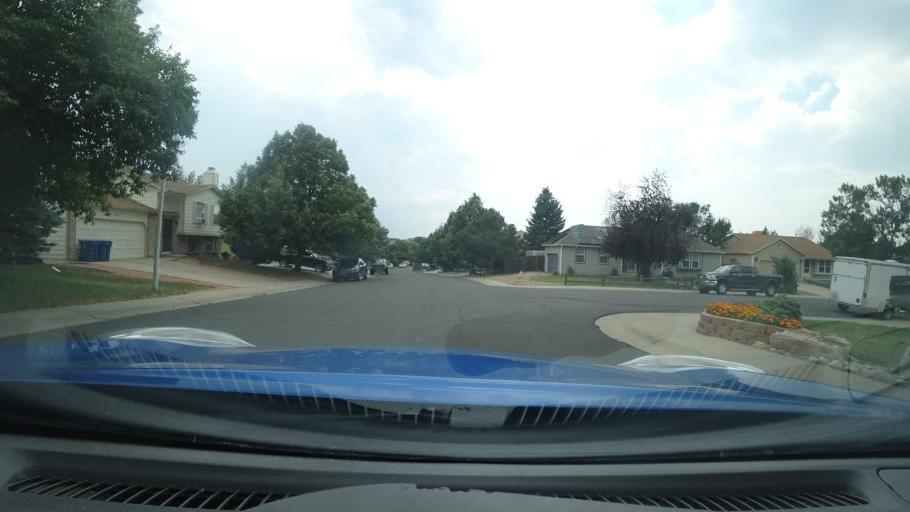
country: US
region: Colorado
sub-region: Adams County
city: Aurora
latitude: 39.6849
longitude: -104.7603
